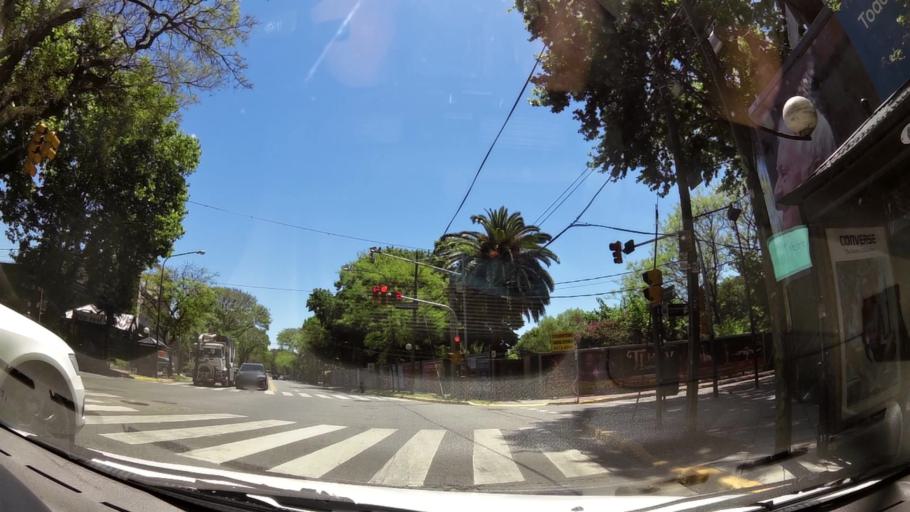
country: AR
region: Buenos Aires
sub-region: Partido de Vicente Lopez
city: Olivos
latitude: -34.4872
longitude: -58.4857
